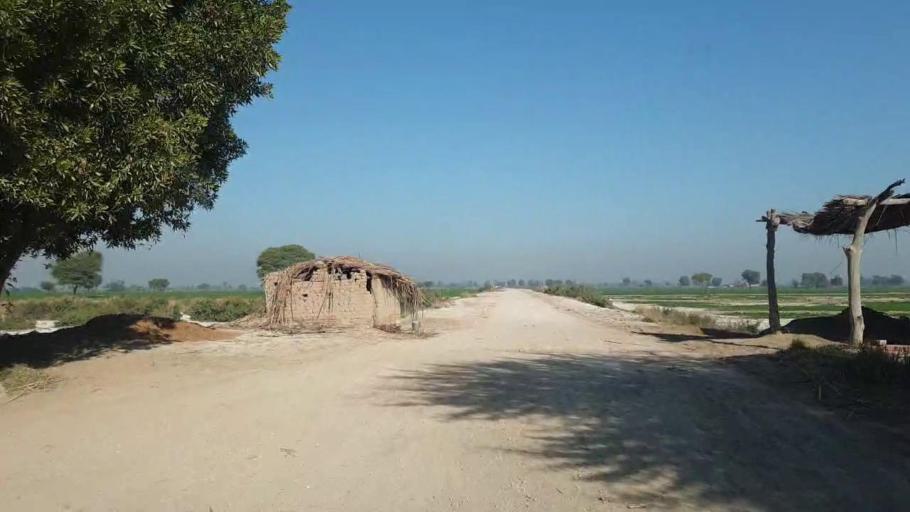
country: PK
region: Sindh
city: Shahdadpur
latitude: 26.0002
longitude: 68.4929
